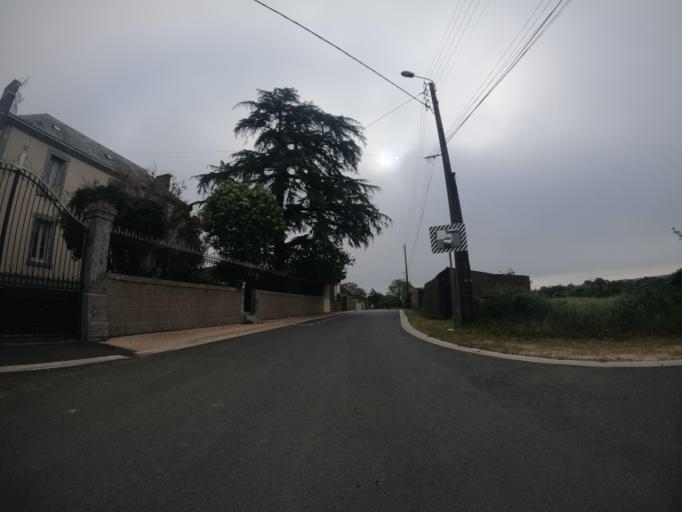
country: FR
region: Poitou-Charentes
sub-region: Departement des Deux-Sevres
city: Mauze-Thouarsais
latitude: 46.8968
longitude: -0.3329
